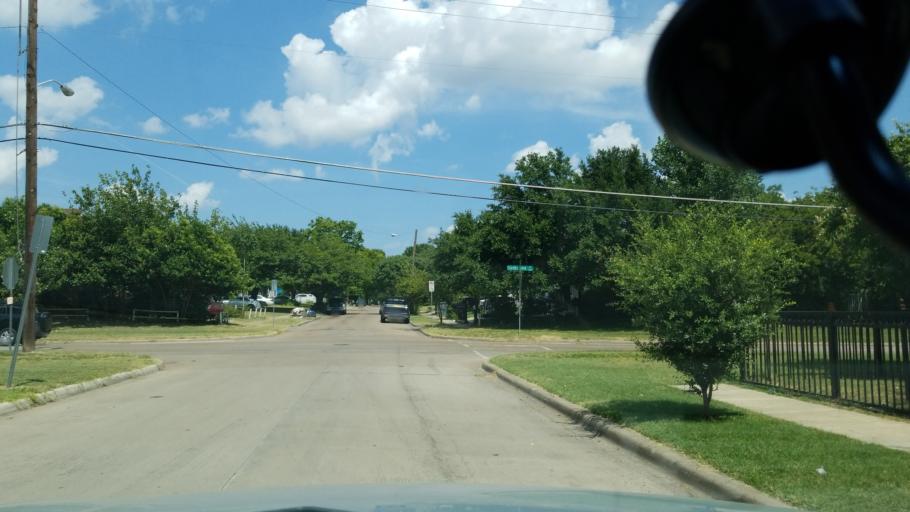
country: US
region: Texas
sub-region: Dallas County
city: Cockrell Hill
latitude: 32.7239
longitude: -96.8779
